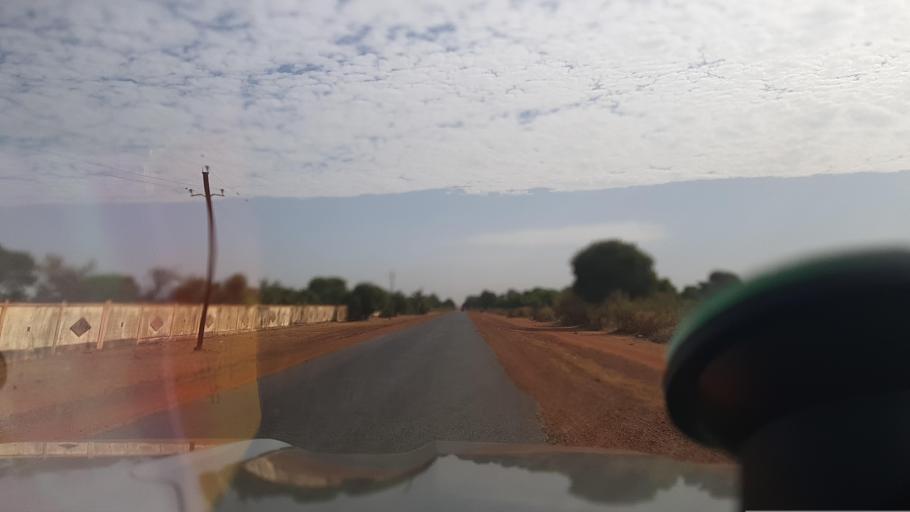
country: ML
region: Segou
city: Segou
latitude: 13.4983
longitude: -6.1585
